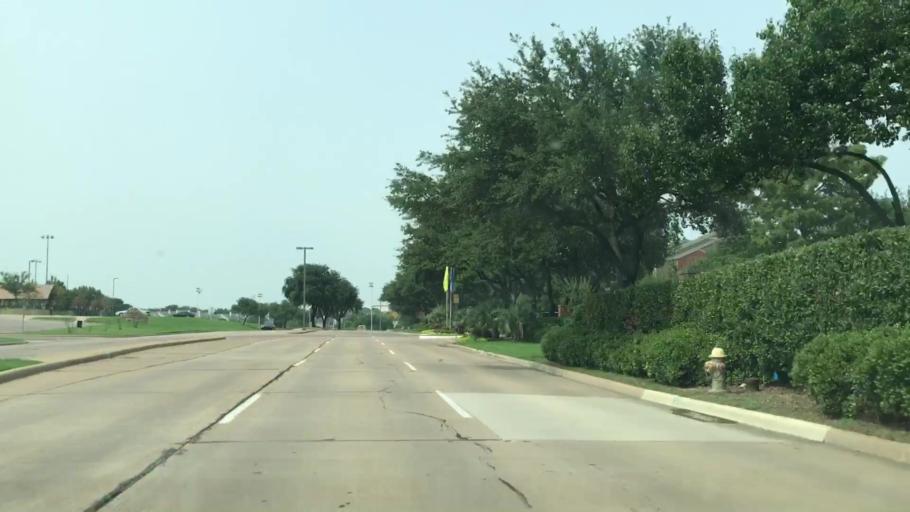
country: US
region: Texas
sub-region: Dallas County
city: Irving
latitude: 32.8611
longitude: -96.9762
